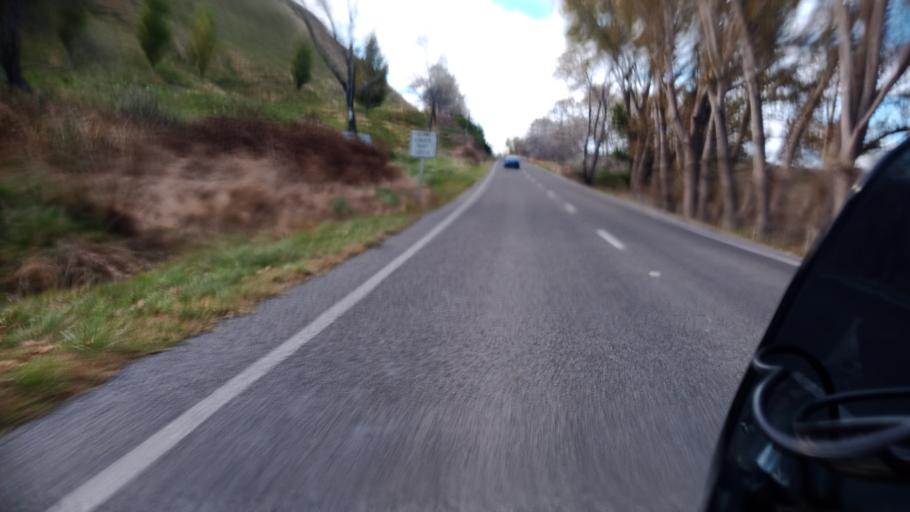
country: NZ
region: Gisborne
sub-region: Gisborne District
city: Gisborne
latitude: -38.8187
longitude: 177.9021
